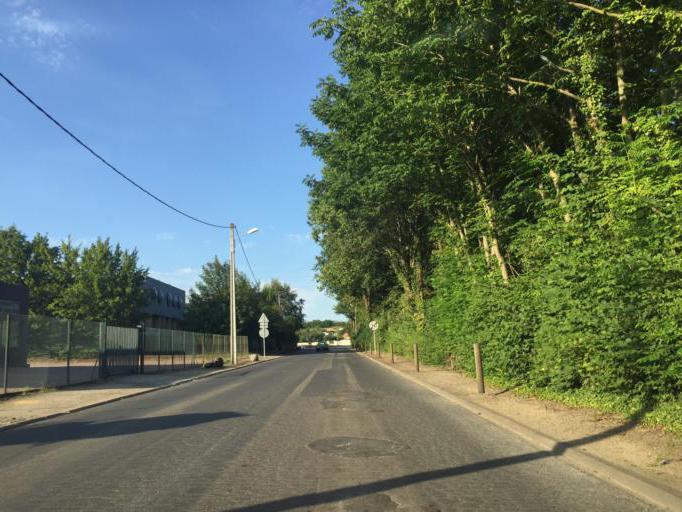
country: FR
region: Auvergne
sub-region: Departement de l'Allier
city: Yzeure
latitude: 46.5415
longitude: 3.3562
